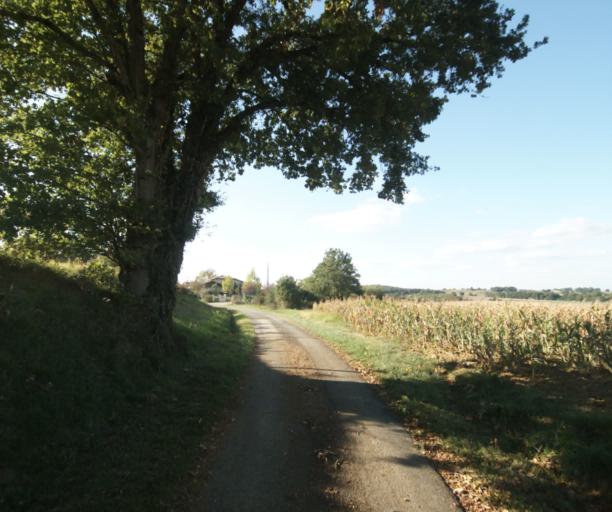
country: FR
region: Midi-Pyrenees
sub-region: Departement du Gers
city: Eauze
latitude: 43.7833
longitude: 0.1353
